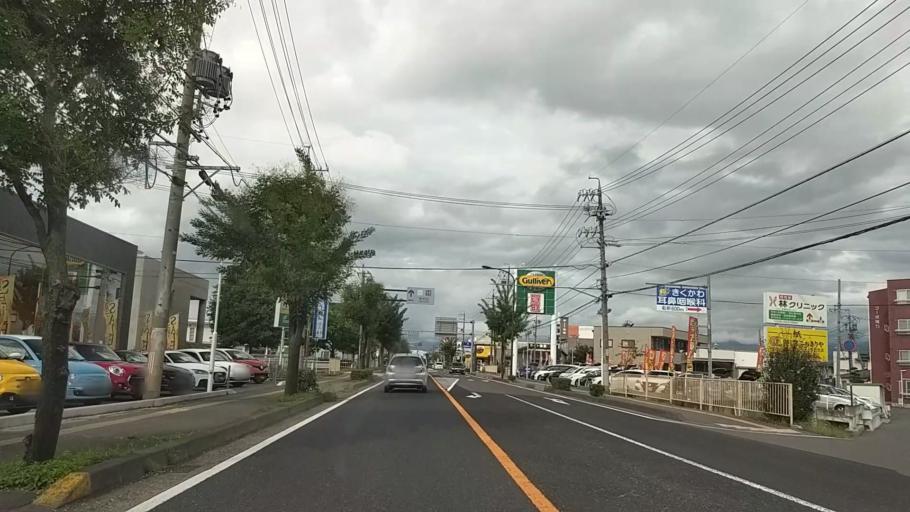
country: JP
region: Nagano
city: Nagano-shi
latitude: 36.6483
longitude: 138.2208
